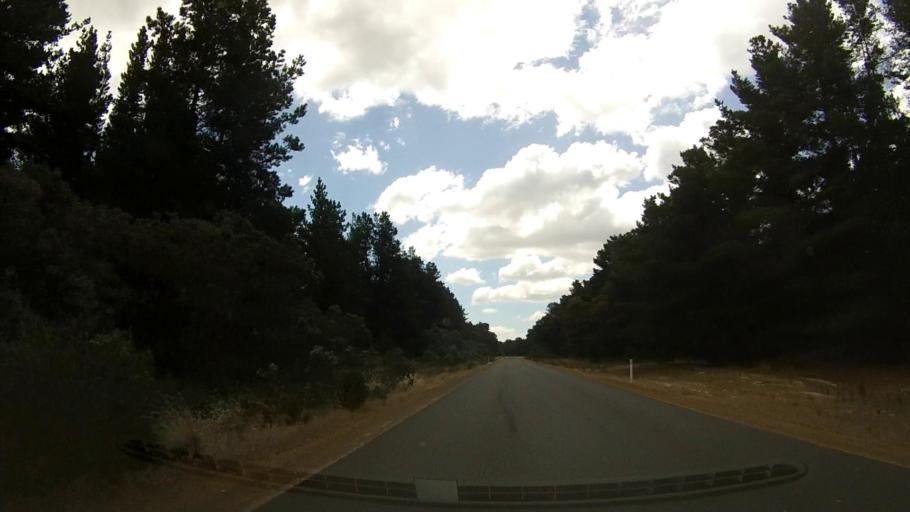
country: AU
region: Tasmania
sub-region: Clarence
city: Seven Mile Beach
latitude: -42.8407
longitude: 147.5313
